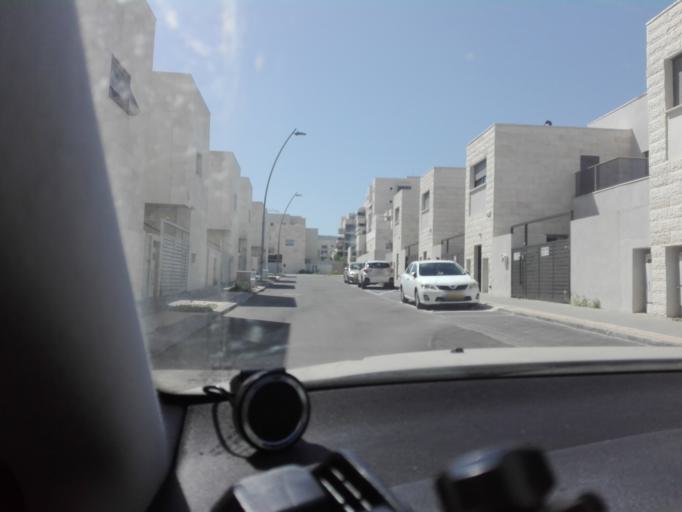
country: IL
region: Central District
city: Bene 'Ayish
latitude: 31.7227
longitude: 34.7435
